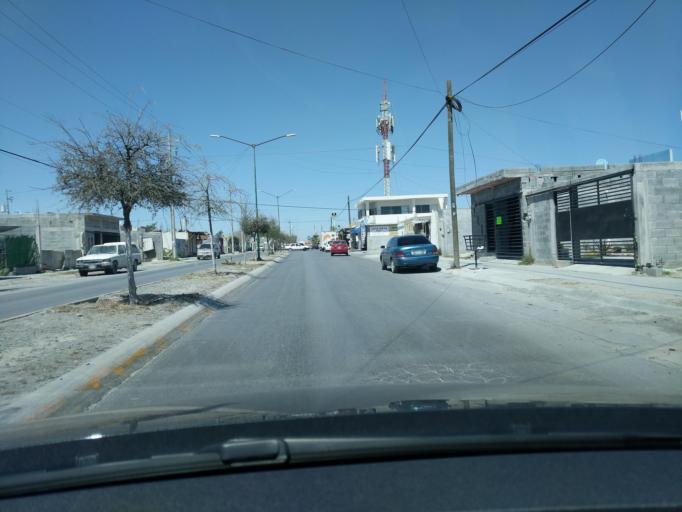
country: MX
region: Nuevo Leon
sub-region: Pesqueria
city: Colinas del Aeropuerto
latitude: 25.8241
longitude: -100.1130
